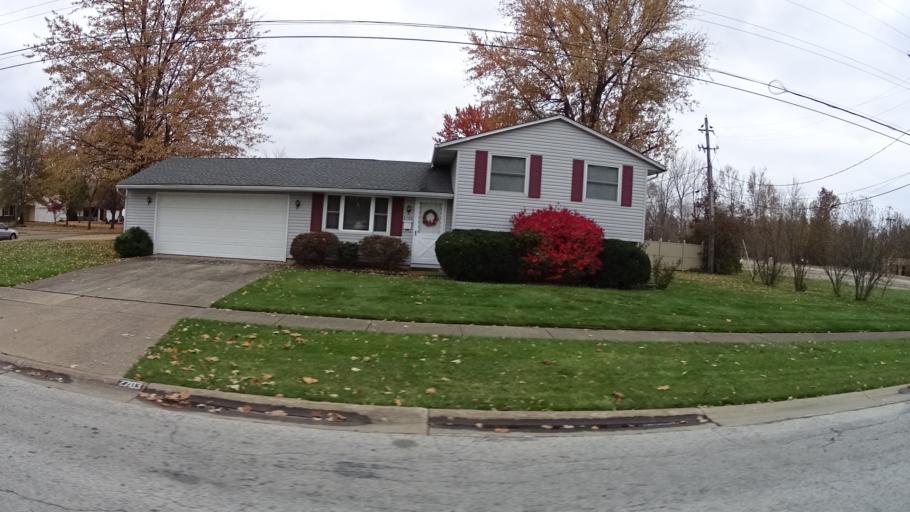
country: US
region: Ohio
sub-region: Lorain County
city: Lorain
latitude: 41.4343
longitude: -82.2081
